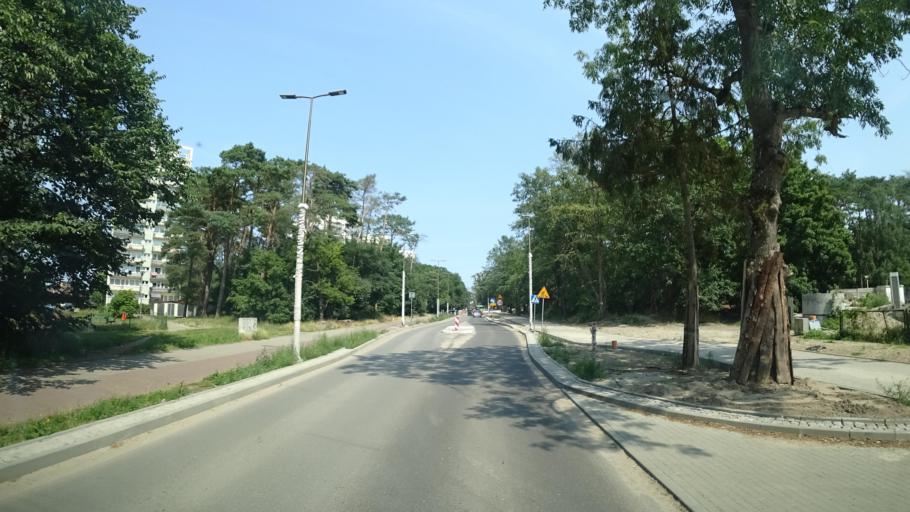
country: PL
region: West Pomeranian Voivodeship
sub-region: Swinoujscie
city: Swinoujscie
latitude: 53.8960
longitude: 14.2263
